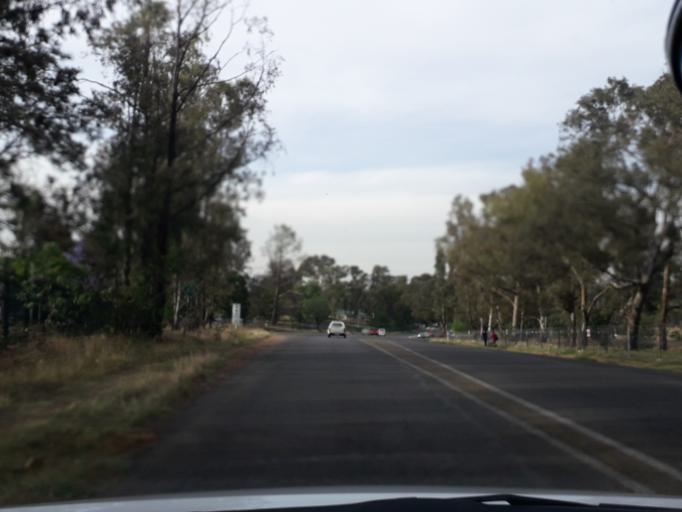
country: ZA
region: Gauteng
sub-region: City of Johannesburg Metropolitan Municipality
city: Modderfontein
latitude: -26.1349
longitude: 28.1181
